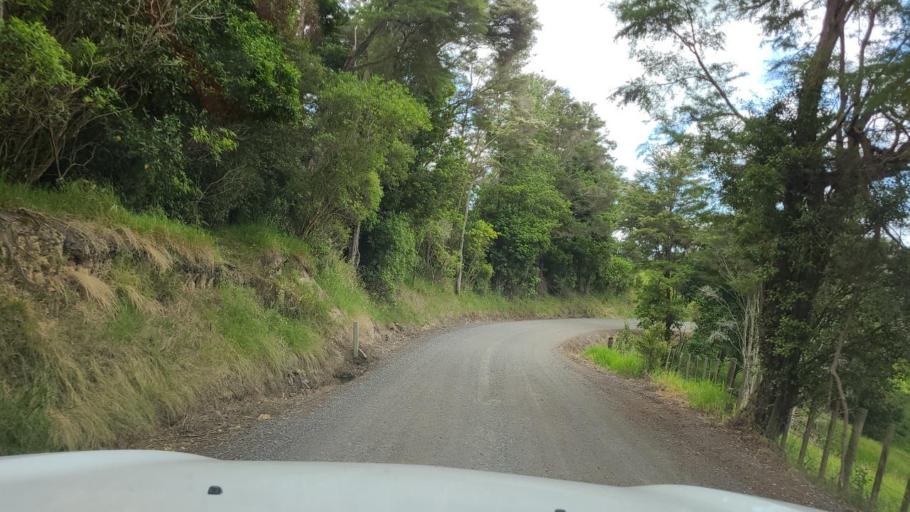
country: NZ
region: Waikato
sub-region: Hauraki District
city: Ngatea
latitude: -37.4467
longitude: 175.4851
